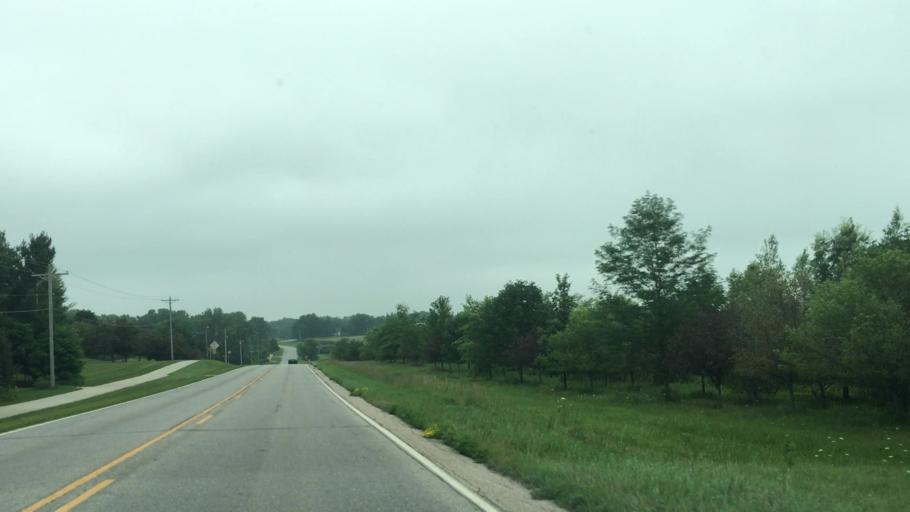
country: US
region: Iowa
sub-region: Johnson County
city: North Liberty
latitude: 41.7286
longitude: -91.5612
